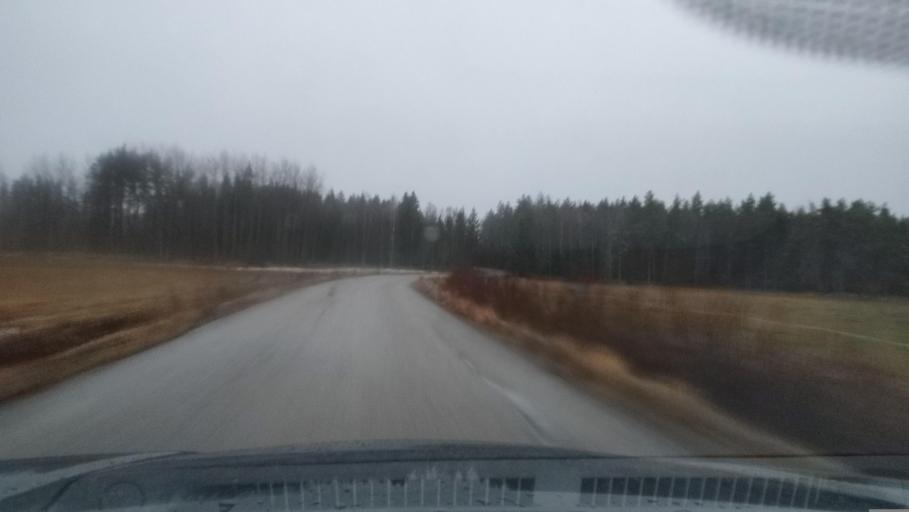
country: FI
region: Southern Ostrobothnia
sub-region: Suupohja
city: Karijoki
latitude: 62.1272
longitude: 21.5912
